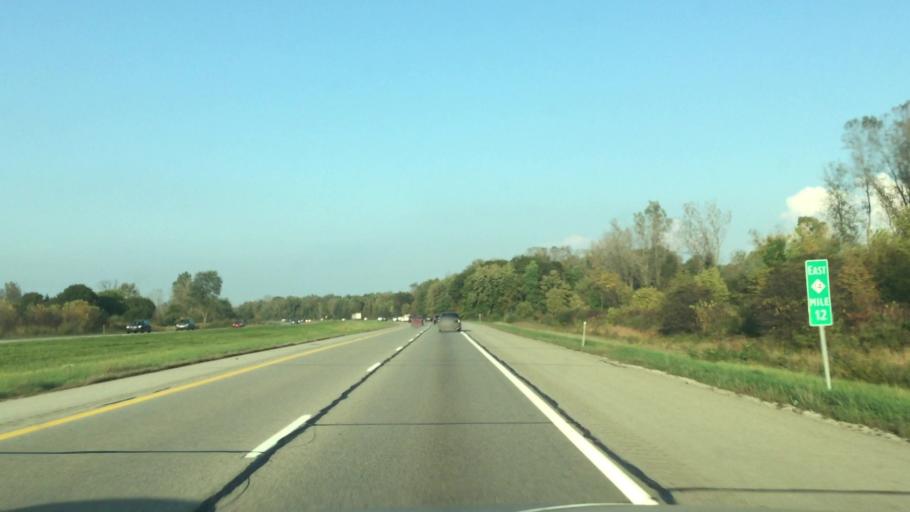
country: US
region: Michigan
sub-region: Washtenaw County
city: Ypsilanti
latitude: 42.3392
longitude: -83.6041
